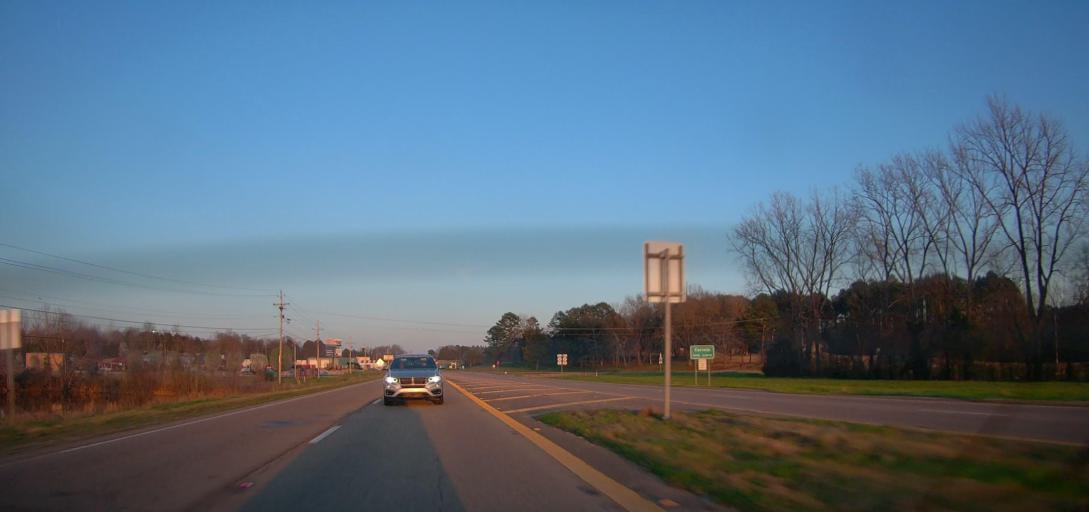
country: US
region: Mississippi
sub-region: Alcorn County
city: Corinth
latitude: 34.9308
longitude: -88.5729
